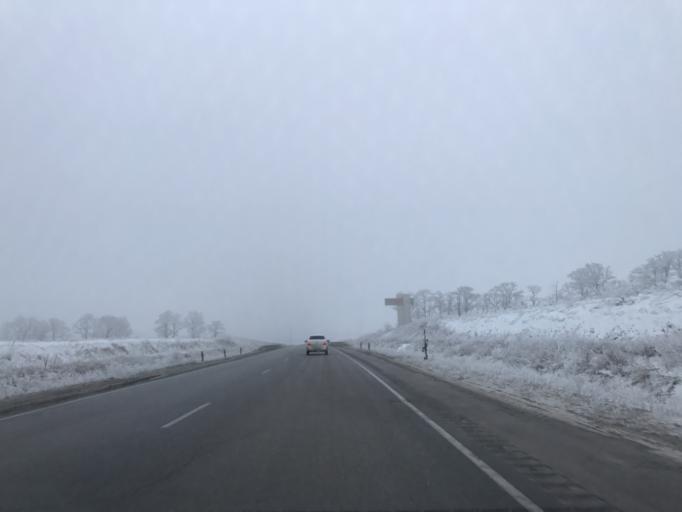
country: RU
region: Rostov
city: Severnyy
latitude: 47.3665
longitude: 39.7008
